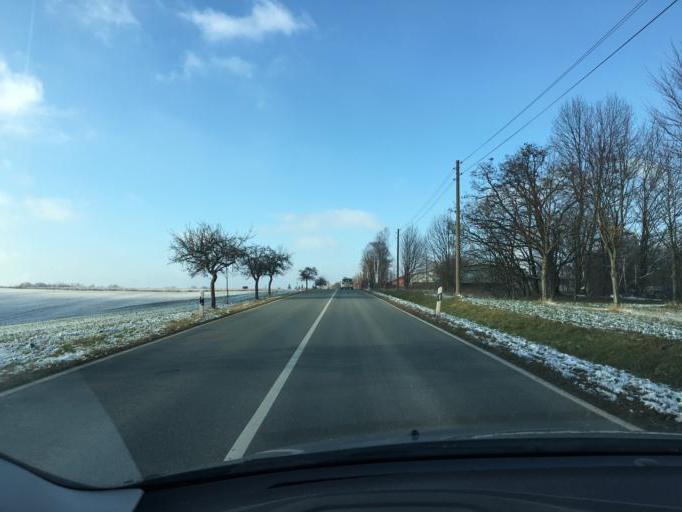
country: DE
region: Saxony
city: Penig
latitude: 50.9397
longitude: 12.6939
